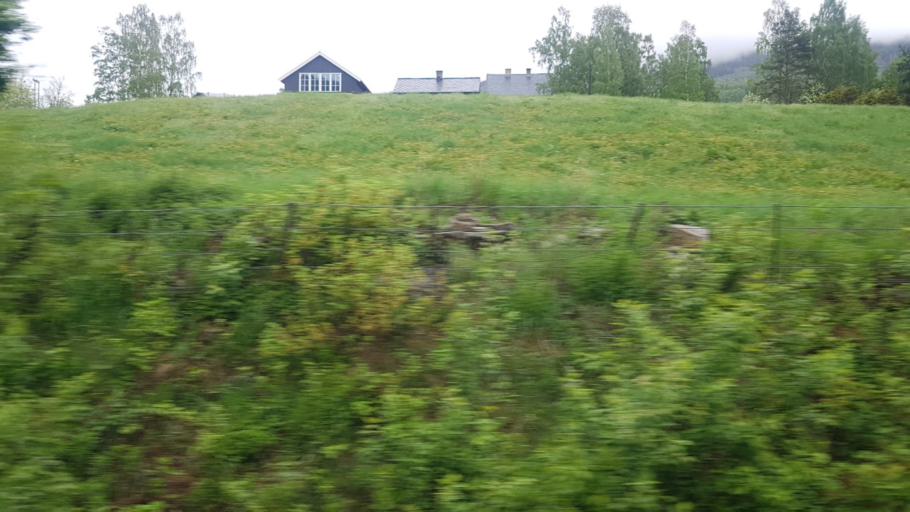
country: NO
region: Oppland
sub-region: Sor-Fron
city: Hundorp
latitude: 61.5578
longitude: 9.9389
